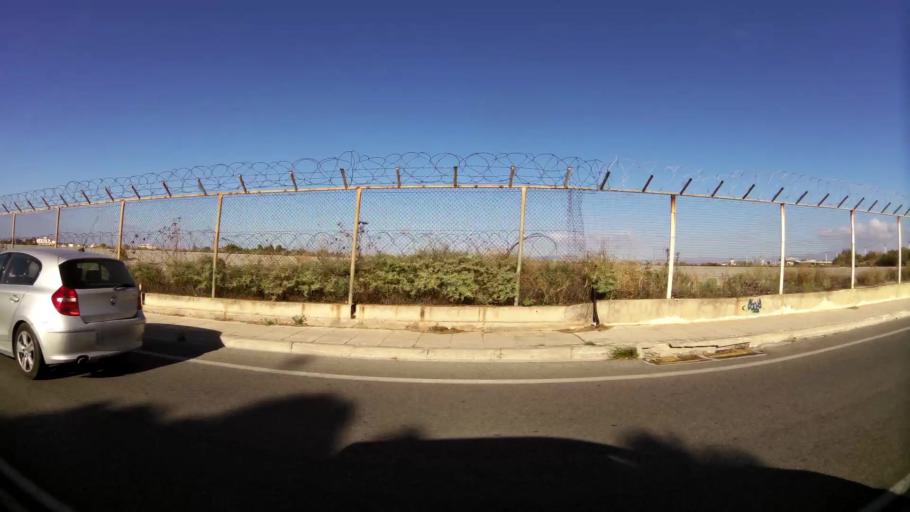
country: GR
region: Attica
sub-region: Nomarchia Athinas
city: Elliniko
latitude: 37.8751
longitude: 23.7422
